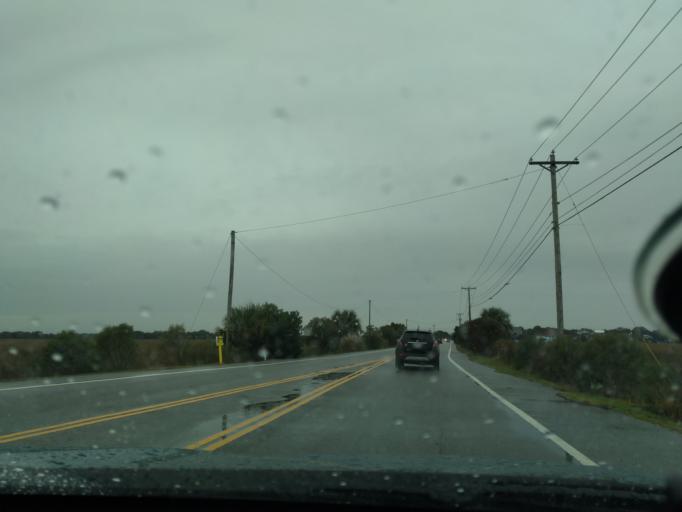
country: US
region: South Carolina
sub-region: Charleston County
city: Folly Beach
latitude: 32.6652
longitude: -79.9454
